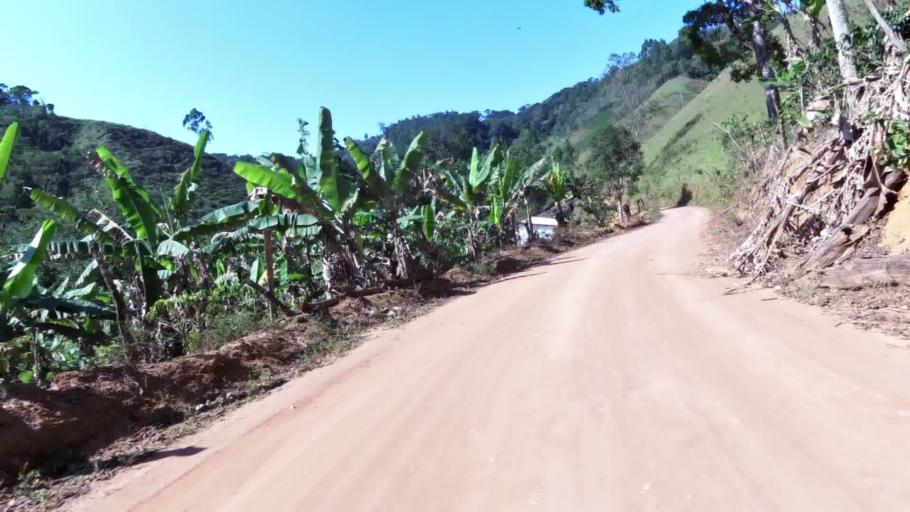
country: BR
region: Espirito Santo
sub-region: Alfredo Chaves
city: Alfredo Chaves
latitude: -20.5631
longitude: -40.7723
